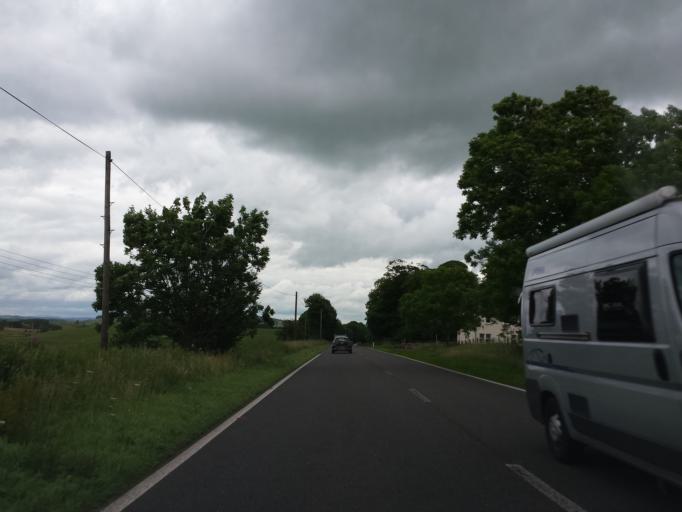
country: GB
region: Scotland
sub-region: Dumfries and Galloway
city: Dalbeattie
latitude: 55.0480
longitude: -3.7856
